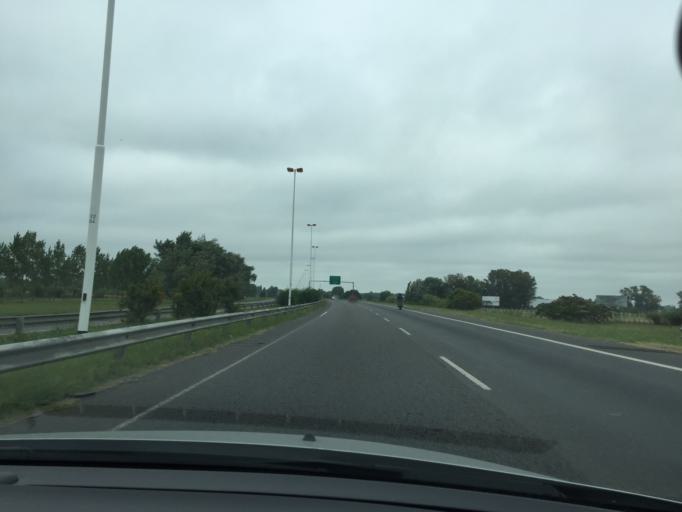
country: AR
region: Buenos Aires
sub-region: Partido de Ezeiza
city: Ezeiza
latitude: -34.8652
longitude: -58.5733
